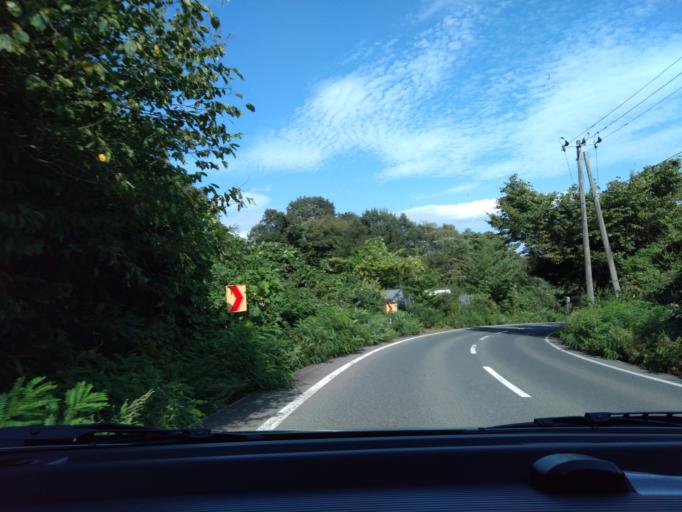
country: JP
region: Iwate
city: Morioka-shi
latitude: 39.6346
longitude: 141.0870
